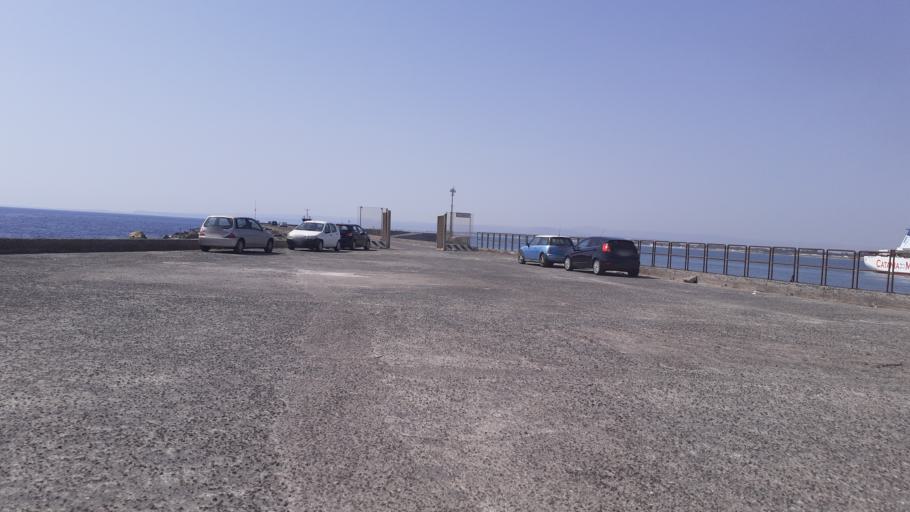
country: IT
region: Sicily
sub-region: Catania
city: Catania
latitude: 37.4914
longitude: 15.0999
